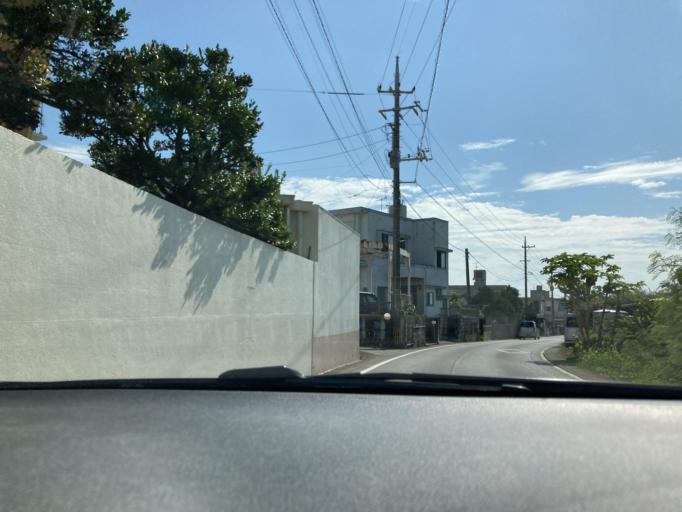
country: JP
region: Okinawa
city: Chatan
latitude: 26.3673
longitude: 127.7424
